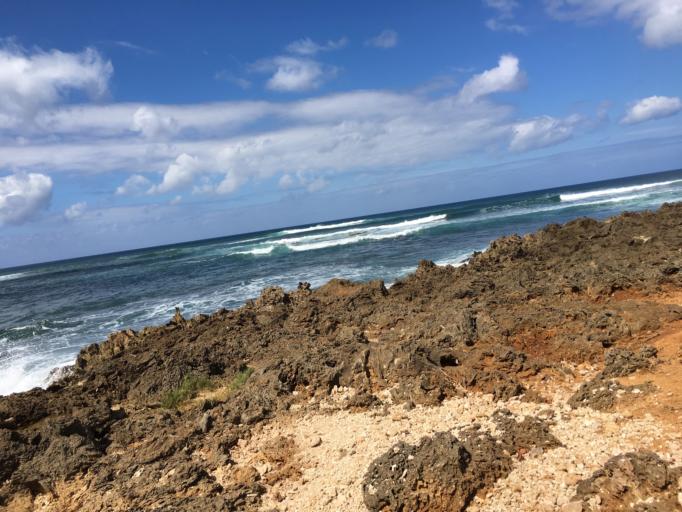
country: US
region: Hawaii
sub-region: Honolulu County
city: Hale'iwa
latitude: 21.5891
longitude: -158.1188
